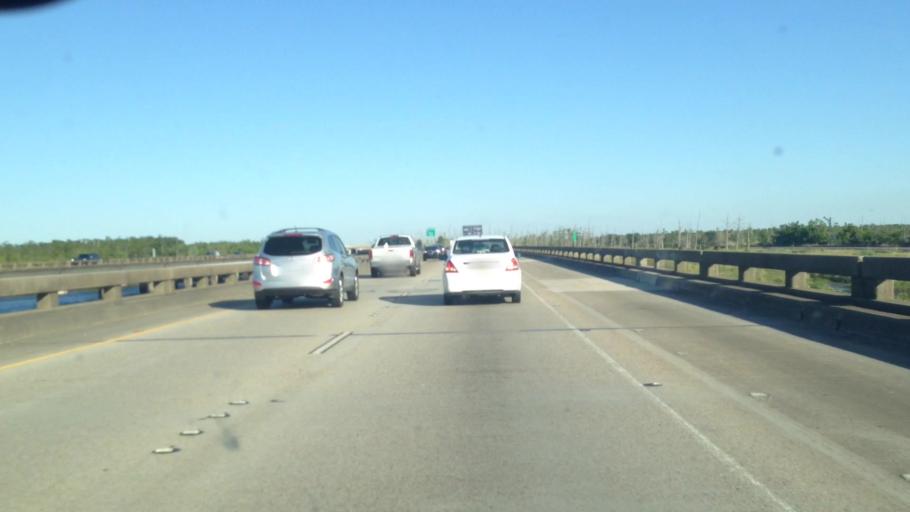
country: US
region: Louisiana
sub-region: Saint Charles Parish
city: Ama
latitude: 30.0130
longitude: -90.3094
